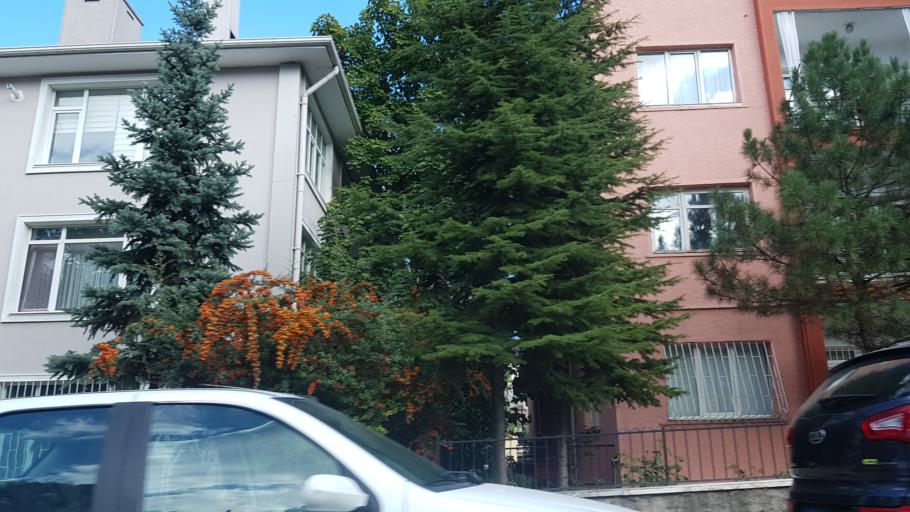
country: TR
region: Ankara
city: Cankaya
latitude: 39.9028
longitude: 32.8673
